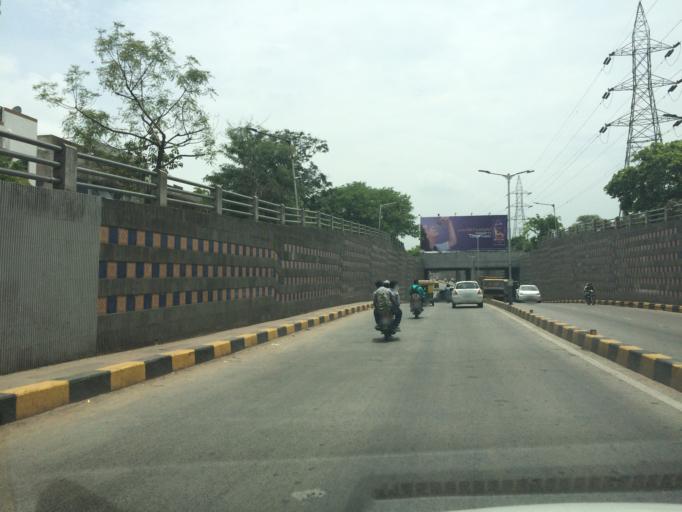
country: IN
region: Gujarat
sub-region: Ahmadabad
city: Ahmedabad
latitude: 23.0669
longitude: 72.5608
